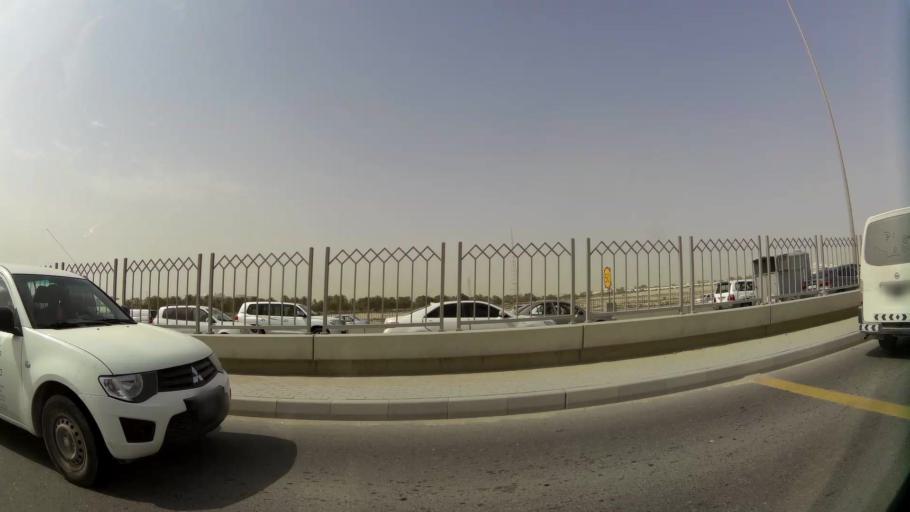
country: QA
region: Baladiyat ad Dawhah
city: Doha
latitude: 25.2877
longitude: 51.4808
